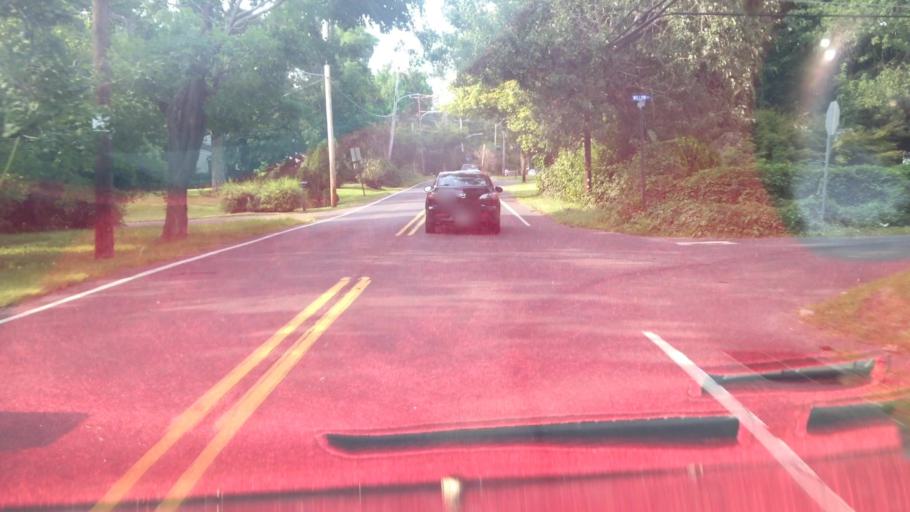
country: US
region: Pennsylvania
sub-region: Bucks County
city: Croydon
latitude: 40.1153
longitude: -74.9023
